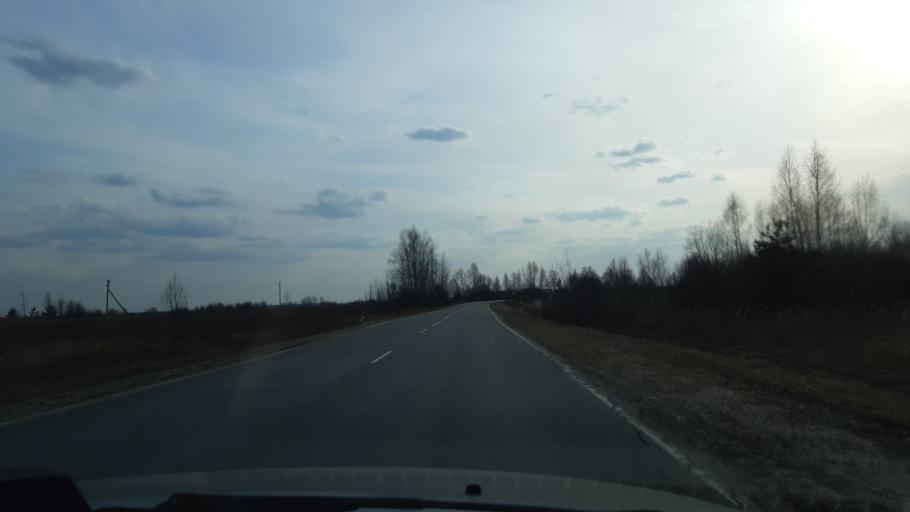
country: RU
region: Vladimir
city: Luknovo
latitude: 56.1921
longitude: 42.0280
